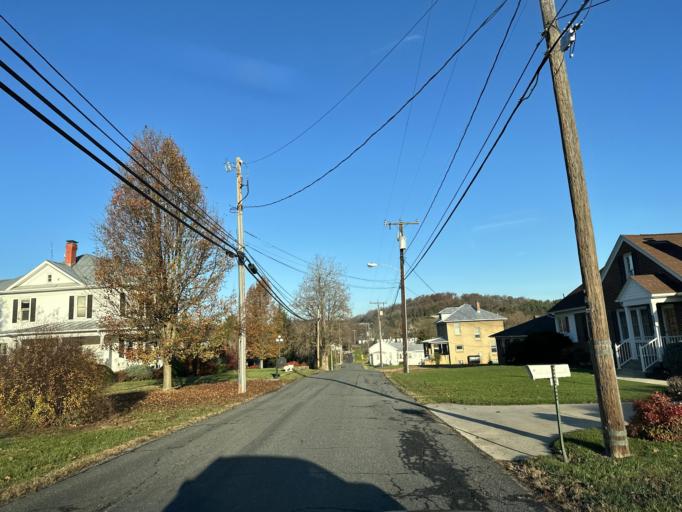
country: US
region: Virginia
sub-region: Augusta County
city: Weyers Cave
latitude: 38.2871
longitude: -78.9123
